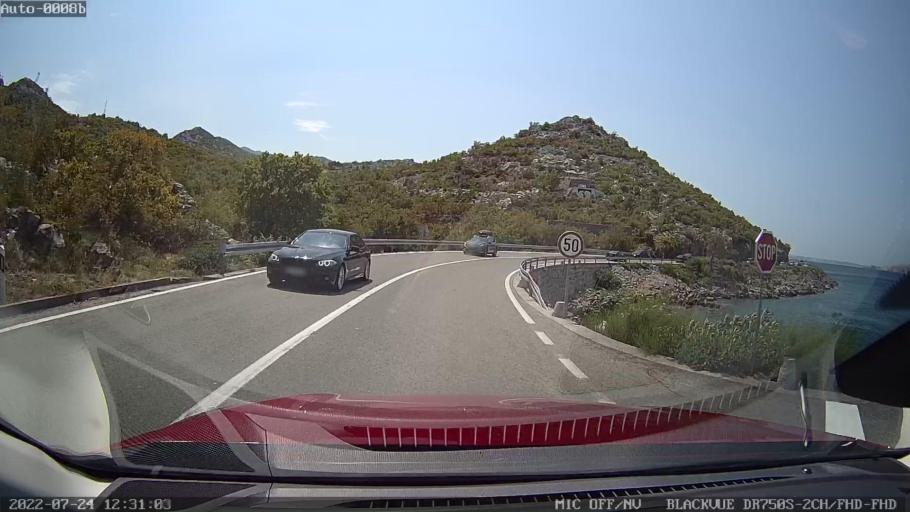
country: HR
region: Licko-Senjska
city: Senj
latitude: 44.9234
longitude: 14.9156
